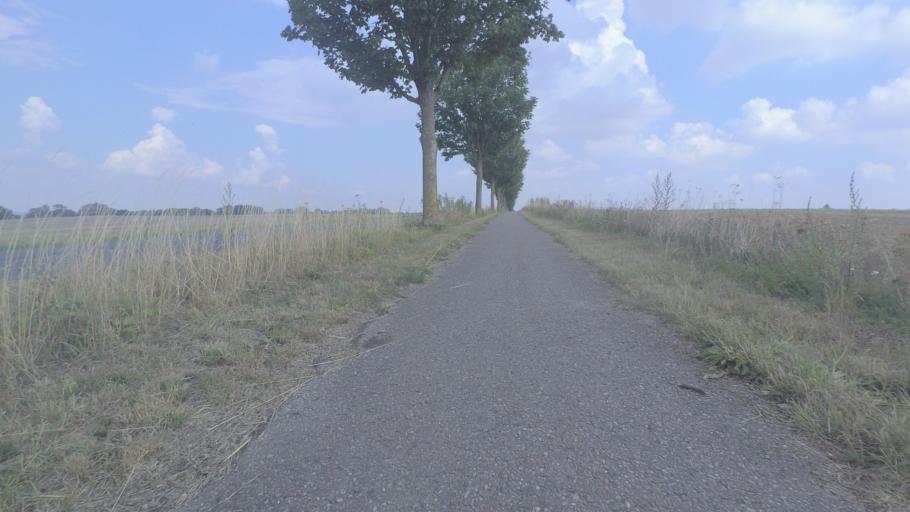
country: DE
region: Mecklenburg-Vorpommern
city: Neukalen
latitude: 53.7695
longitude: 12.8513
